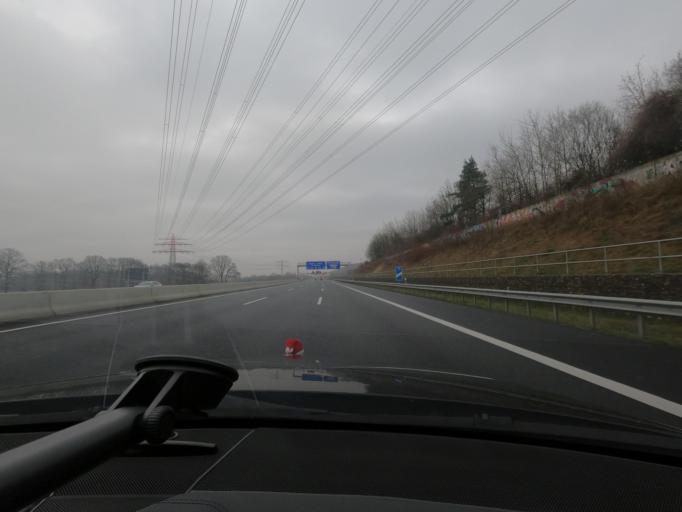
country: DE
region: Schleswig-Holstein
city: Bonningstedt
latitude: 53.6509
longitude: 9.9304
